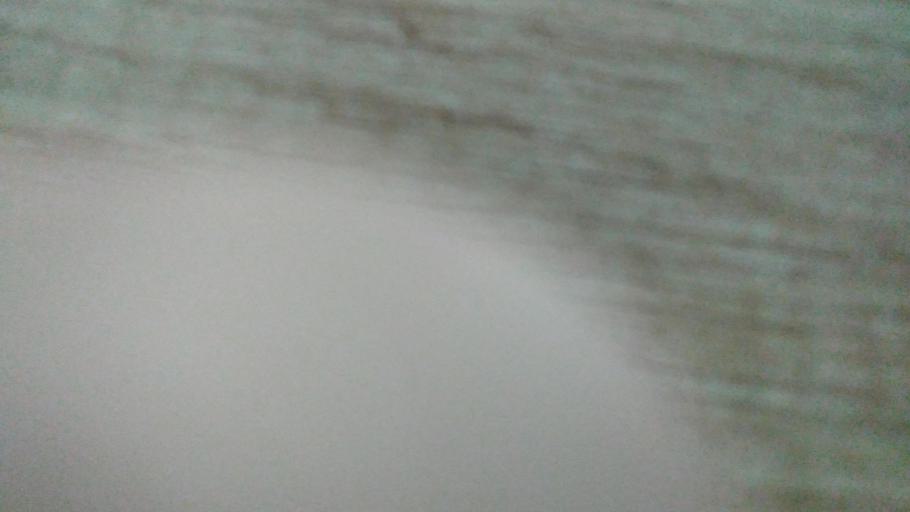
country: RU
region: Moskovskaya
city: Pushchino
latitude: 54.8171
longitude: 37.5701
